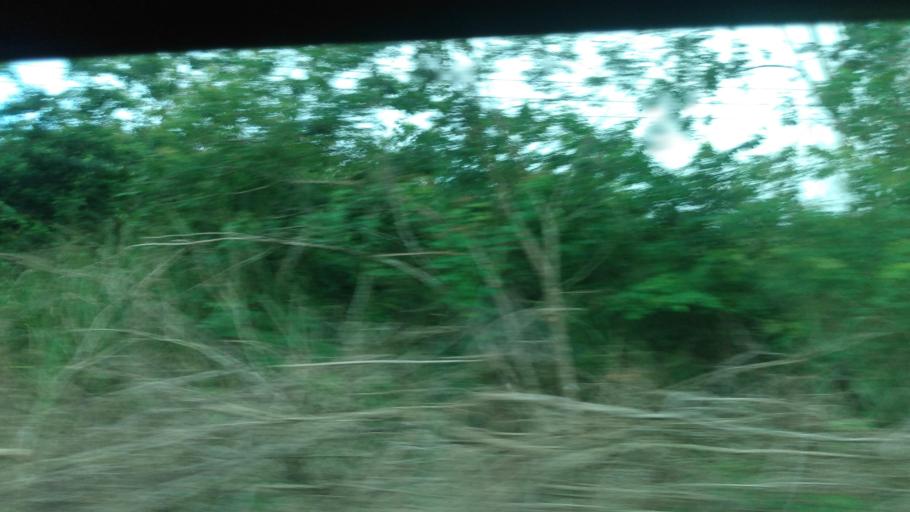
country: BR
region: Pernambuco
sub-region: Quipapa
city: Quipapa
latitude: -8.7883
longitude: -35.9729
